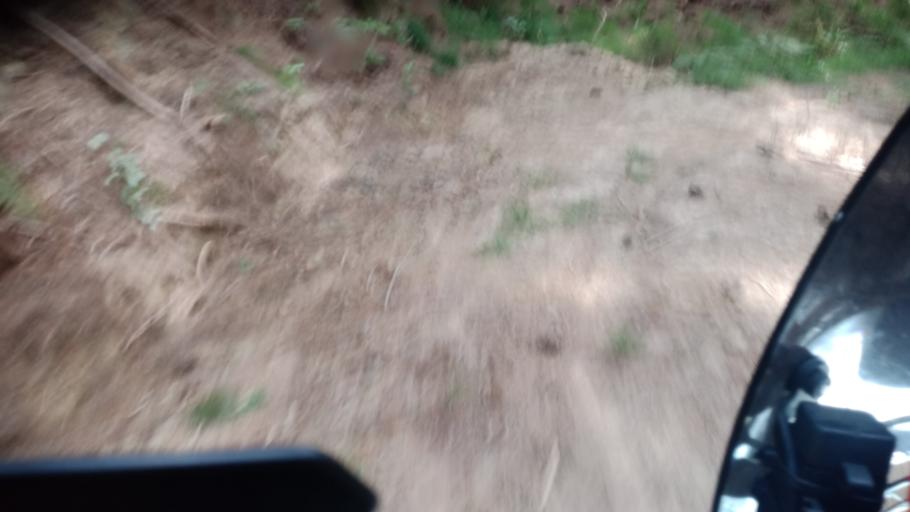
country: NZ
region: Gisborne
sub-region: Gisborne District
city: Gisborne
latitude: -38.4592
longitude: 177.9274
